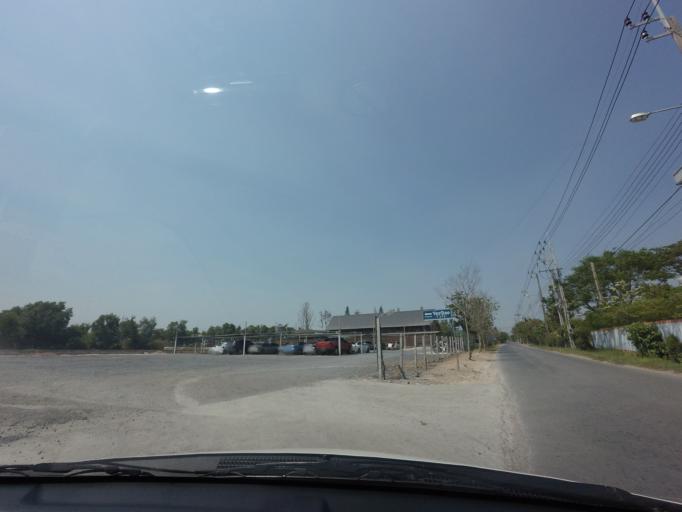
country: TH
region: Bangkok
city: Nong Chok
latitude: 13.8640
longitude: 100.8530
